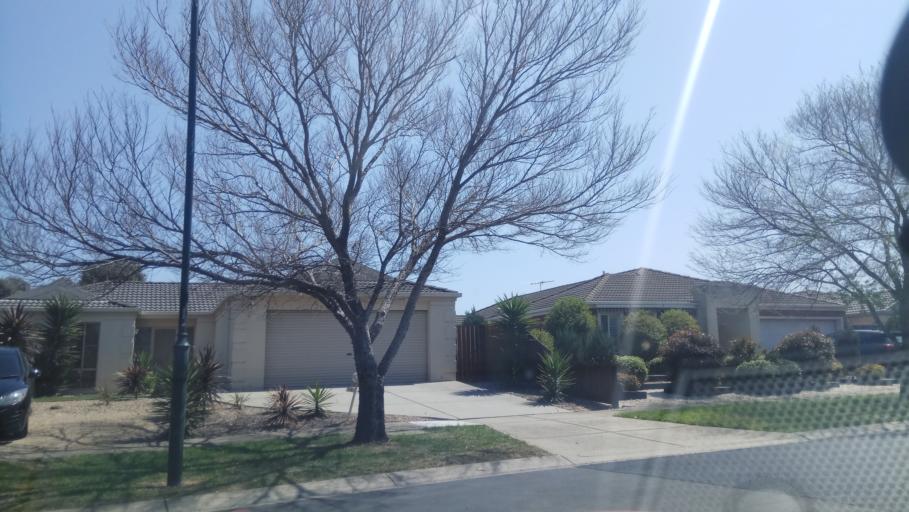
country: AU
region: Victoria
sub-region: Wyndham
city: Williams Landing
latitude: -37.8840
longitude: 144.7503
